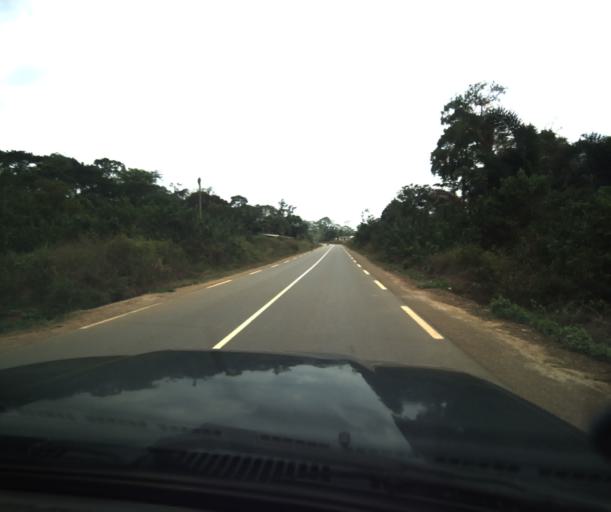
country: CM
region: Centre
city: Akono
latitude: 3.5627
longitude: 11.3032
